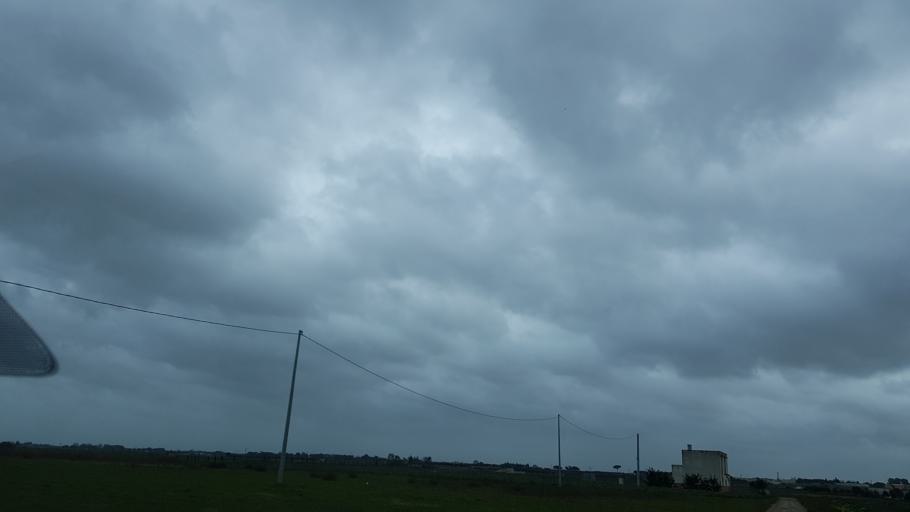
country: IT
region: Apulia
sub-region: Provincia di Brindisi
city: Brindisi
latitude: 40.6599
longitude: 17.8641
